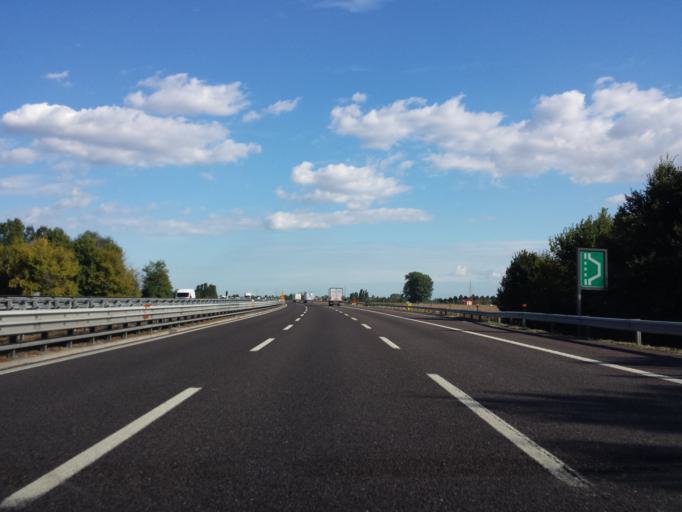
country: IT
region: Veneto
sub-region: Provincia di Padova
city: Bosco
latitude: 45.4566
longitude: 11.7898
